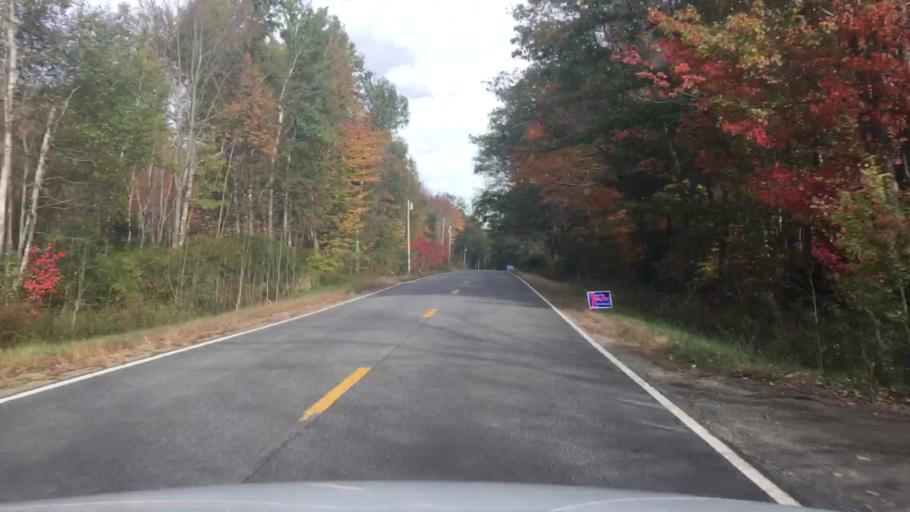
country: US
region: Maine
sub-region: Waldo County
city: Searsmont
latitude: 44.3457
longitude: -69.1397
